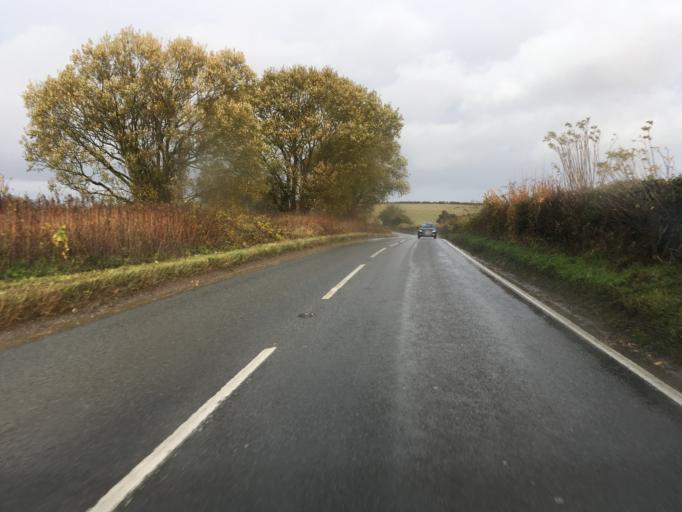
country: GB
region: England
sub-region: South Gloucestershire
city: Cold Ashton
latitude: 51.4637
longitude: -2.3719
